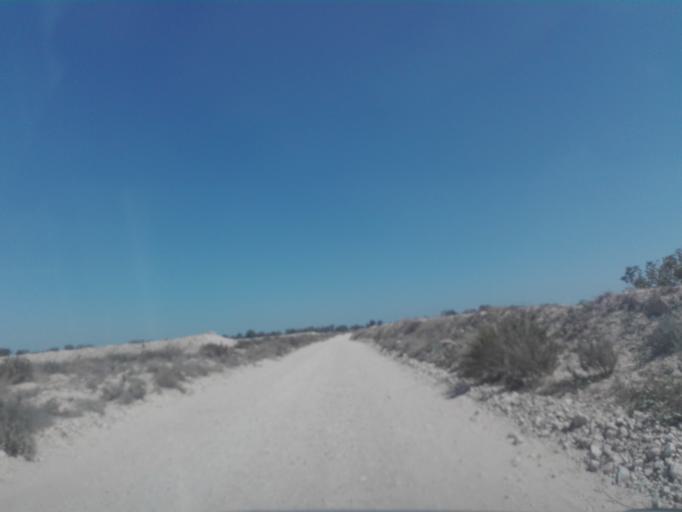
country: TN
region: Qabis
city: Gabes
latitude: 33.8728
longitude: 10.0175
